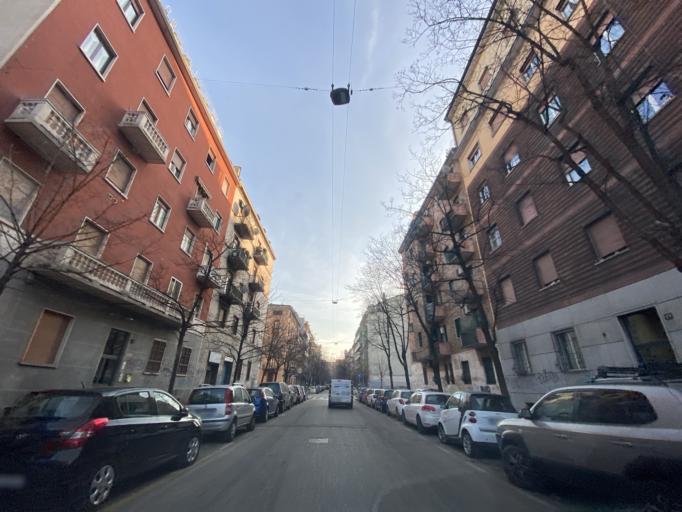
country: IT
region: Lombardy
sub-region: Citta metropolitana di Milano
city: Sesto San Giovanni
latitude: 45.4884
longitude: 9.2330
